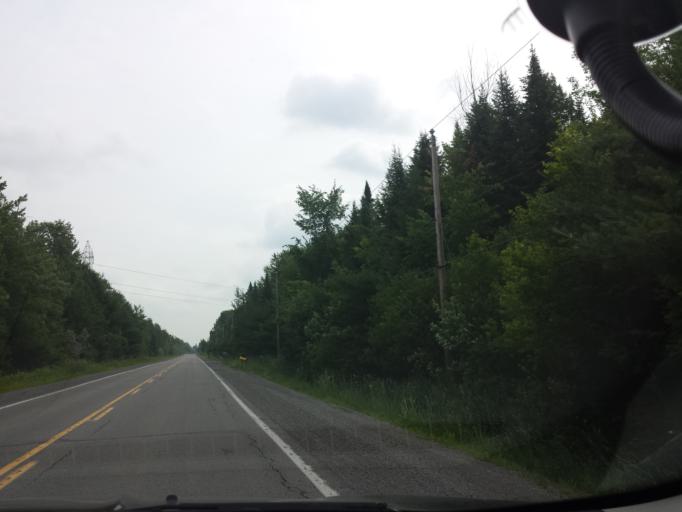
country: CA
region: Ontario
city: Ottawa
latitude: 45.3607
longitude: -75.5326
